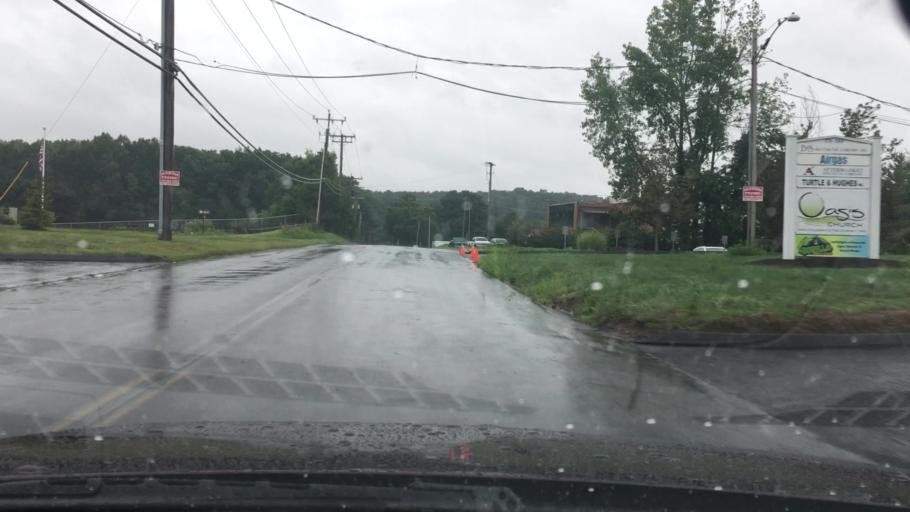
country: US
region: Connecticut
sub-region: New Haven County
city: Cheshire Village
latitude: 41.5332
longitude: -72.8985
